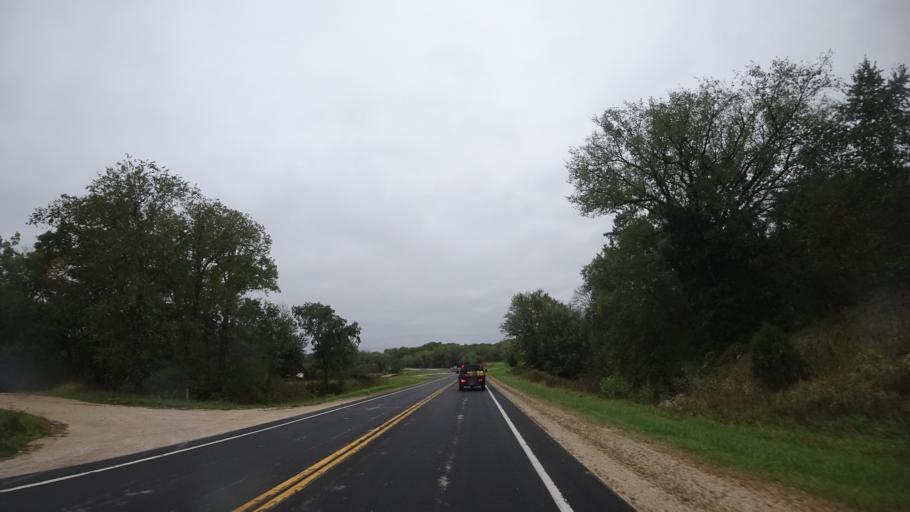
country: US
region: Wisconsin
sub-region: Grant County
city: Boscobel
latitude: 43.1116
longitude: -90.8004
